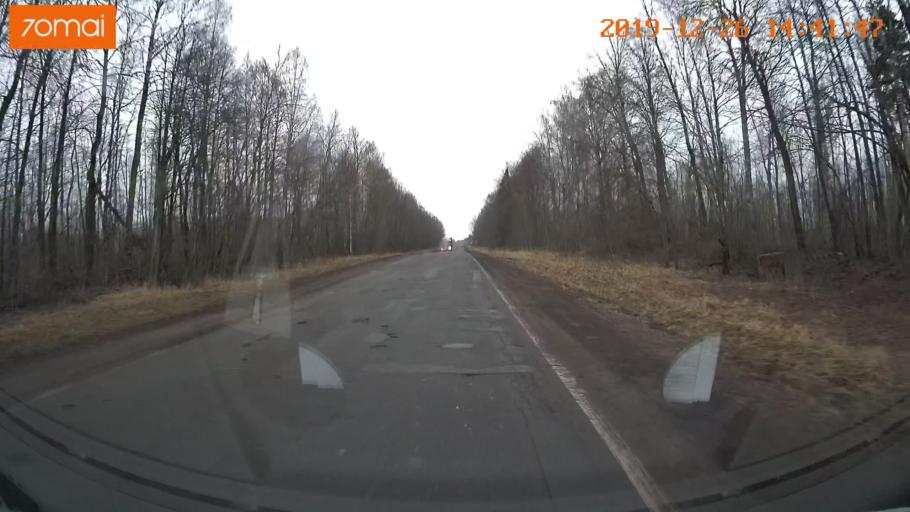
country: RU
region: Jaroslavl
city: Poshekhon'ye
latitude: 58.3685
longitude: 39.0235
